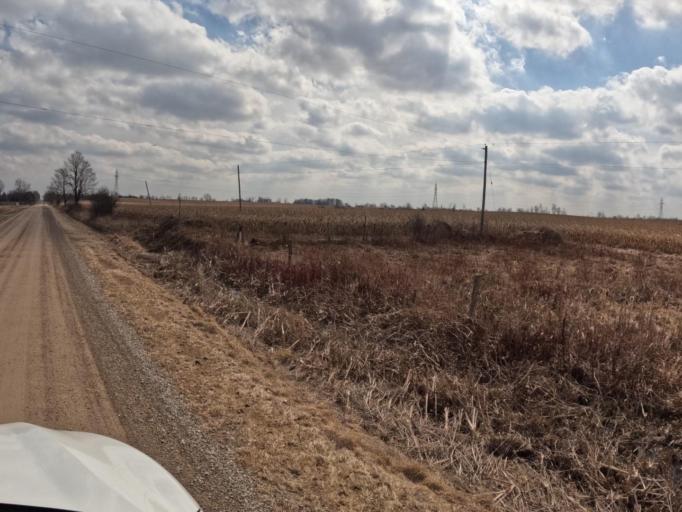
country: CA
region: Ontario
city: Shelburne
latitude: 43.9606
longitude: -80.2818
